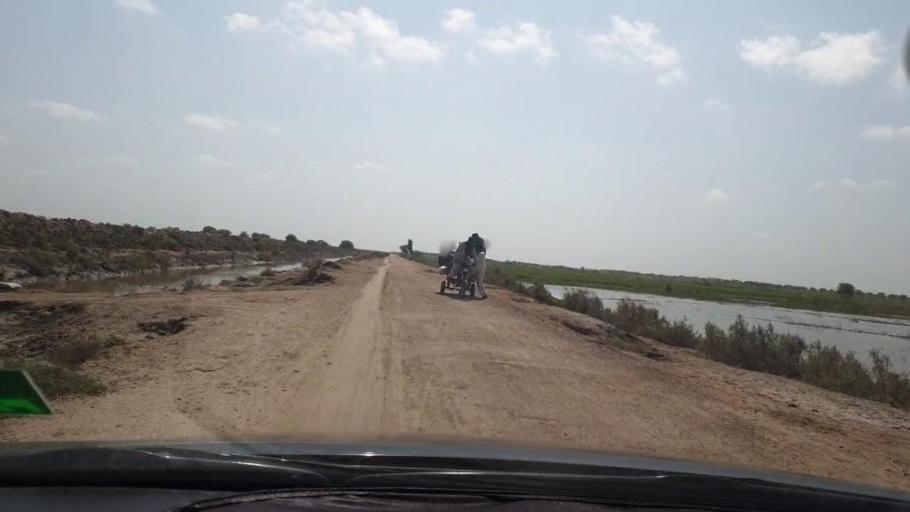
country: PK
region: Sindh
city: Tando Bago
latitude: 24.8402
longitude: 69.0453
